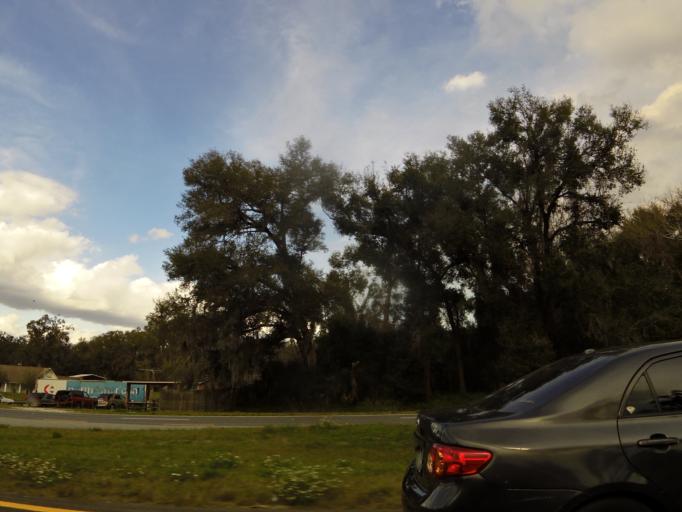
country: US
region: Florida
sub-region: Volusia County
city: De Leon Springs
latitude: 29.1102
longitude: -81.3479
